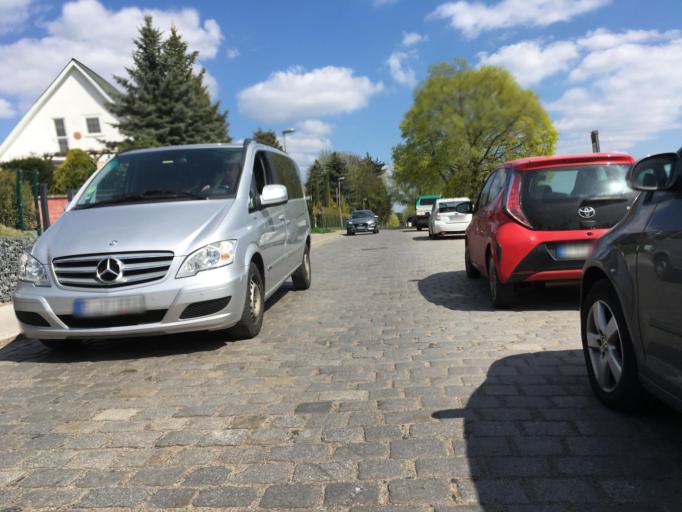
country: DE
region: Berlin
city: Lubars
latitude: 52.6123
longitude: 13.3592
